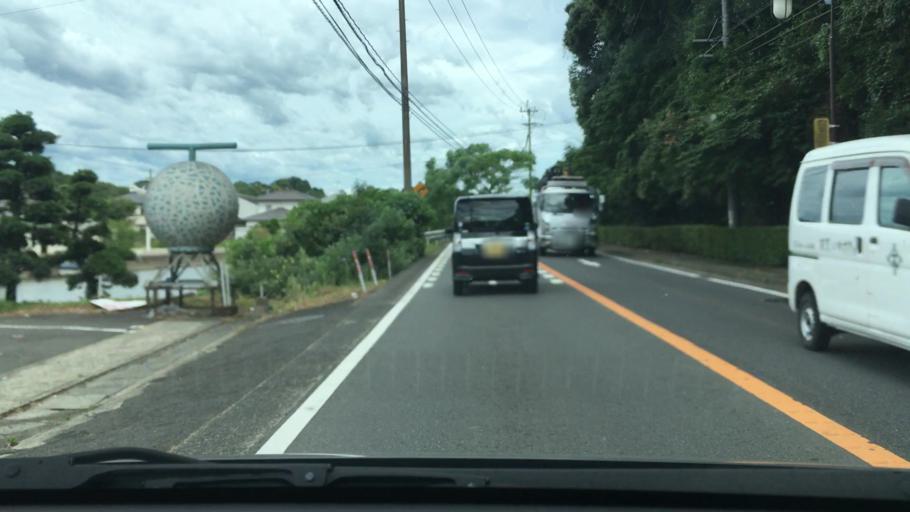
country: JP
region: Nagasaki
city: Togitsu
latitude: 32.8872
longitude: 129.7890
